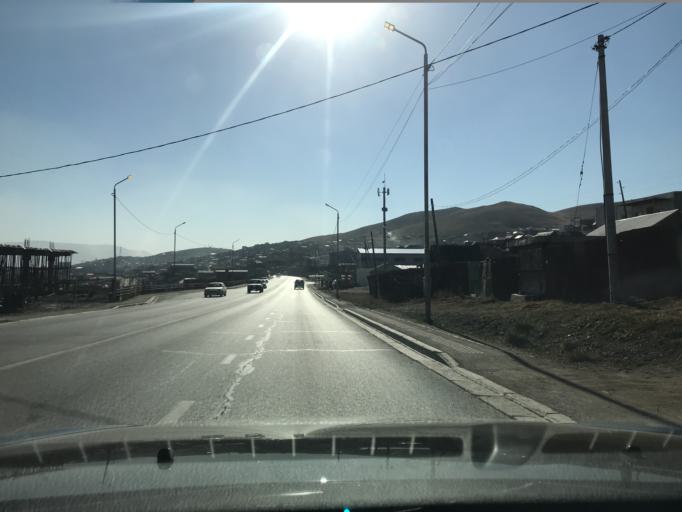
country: MN
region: Ulaanbaatar
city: Ulaanbaatar
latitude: 47.9813
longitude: 106.9217
